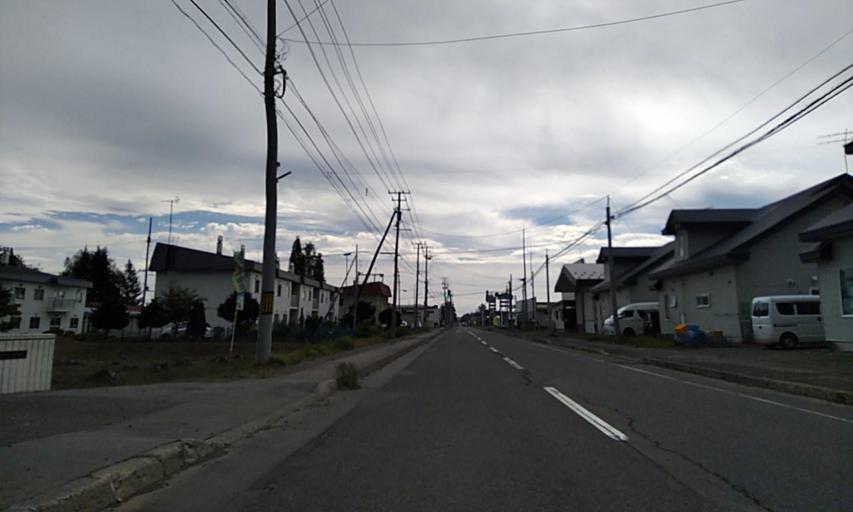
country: JP
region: Hokkaido
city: Obihiro
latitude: 42.8505
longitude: 143.1632
